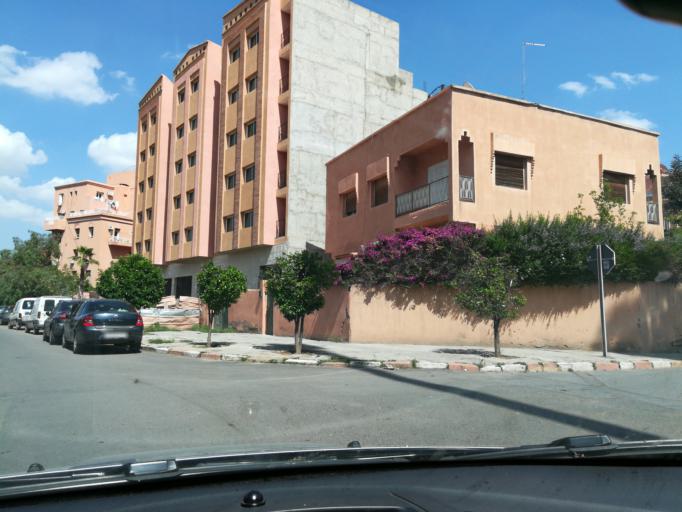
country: MA
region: Marrakech-Tensift-Al Haouz
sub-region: Marrakech
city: Marrakesh
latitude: 31.6348
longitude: -8.0055
